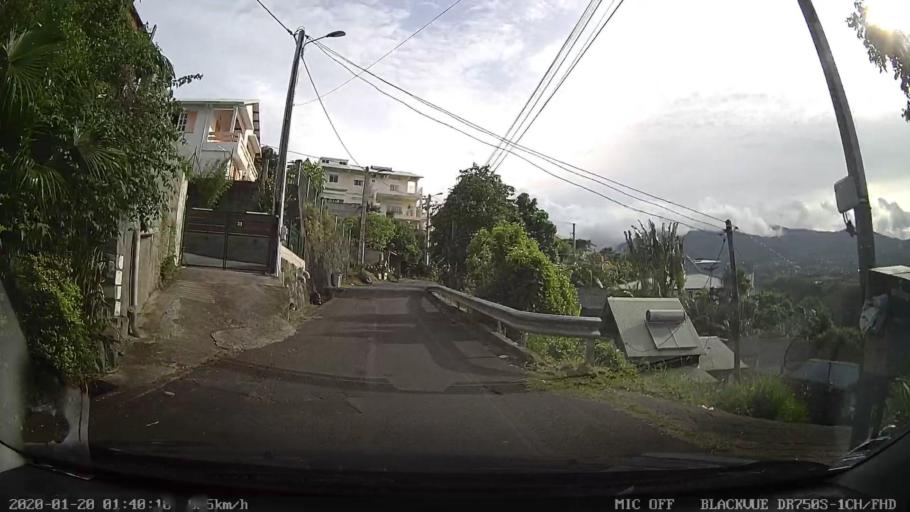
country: RE
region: Reunion
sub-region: Reunion
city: Sainte-Marie
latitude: -20.9215
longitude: 55.5150
